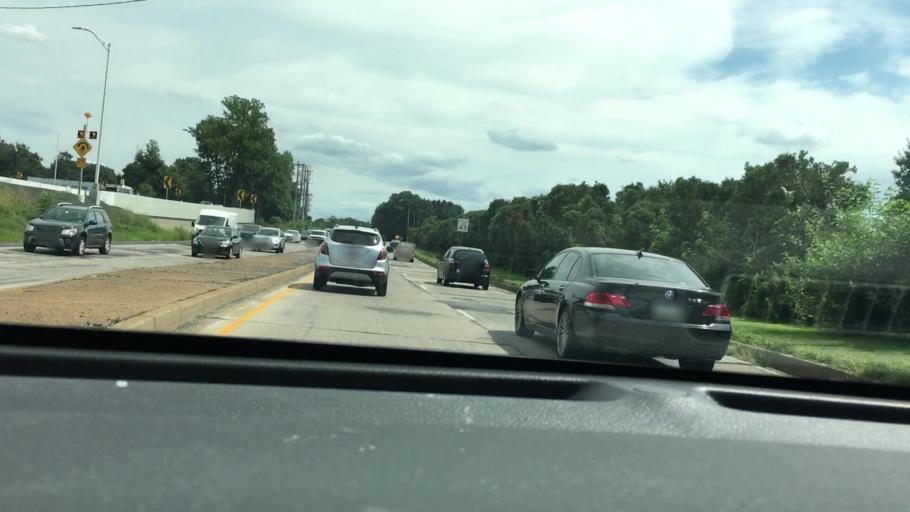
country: US
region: Pennsylvania
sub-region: Bucks County
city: Trevose
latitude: 40.1318
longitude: -74.9746
